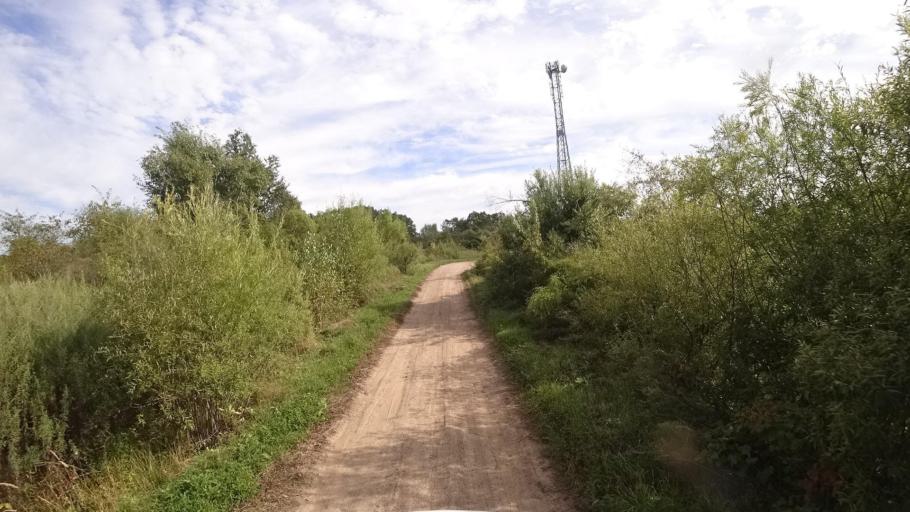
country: RU
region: Primorskiy
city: Dostoyevka
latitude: 44.3232
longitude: 133.4809
